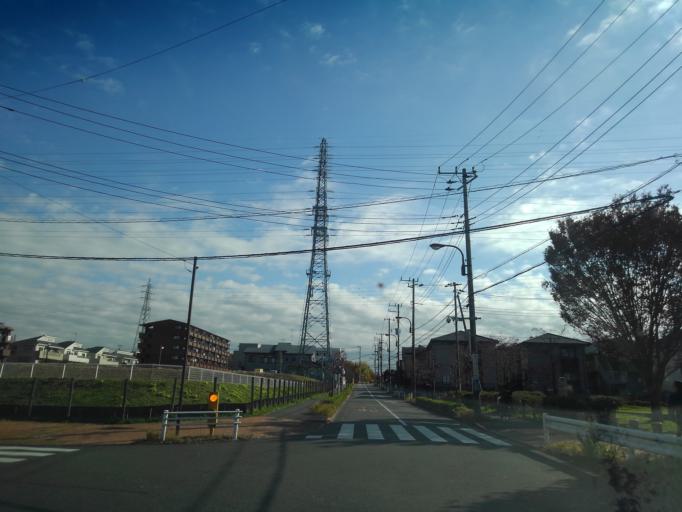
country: JP
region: Tokyo
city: Hachioji
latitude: 35.6017
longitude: 139.3671
